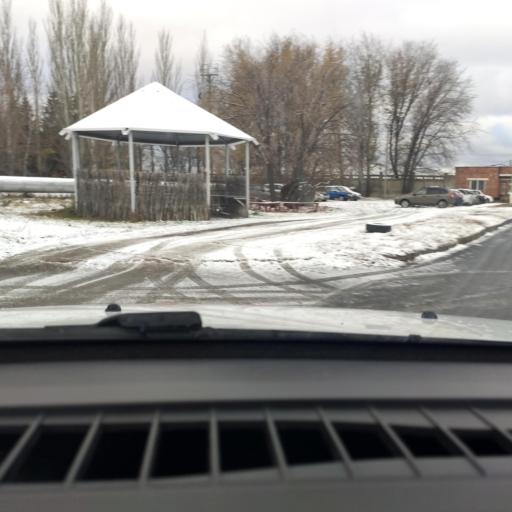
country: RU
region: Samara
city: Podstepki
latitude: 53.5865
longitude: 49.2129
